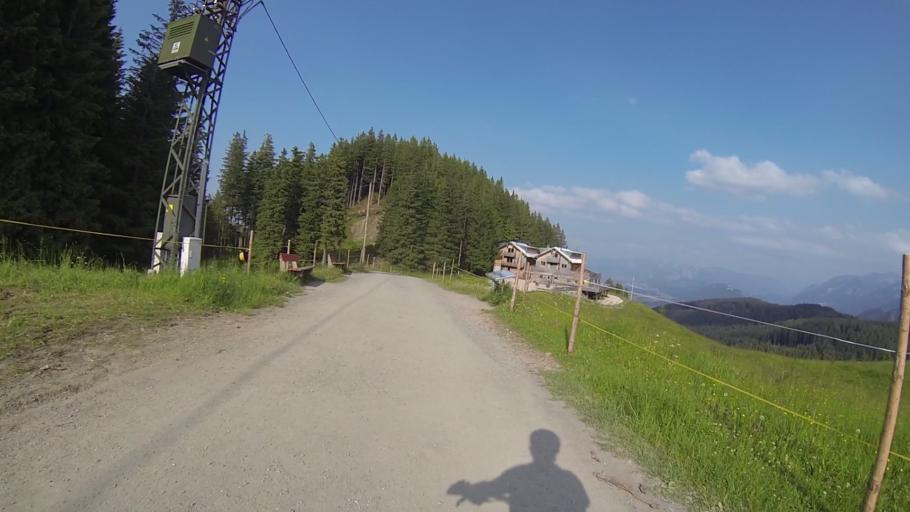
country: DE
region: Bavaria
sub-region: Swabia
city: Nesselwang
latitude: 47.5986
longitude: 10.5025
